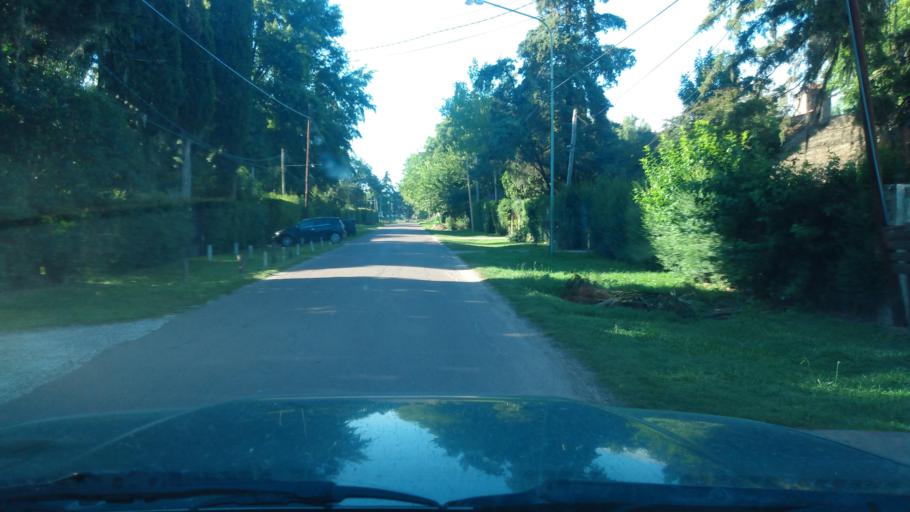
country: AR
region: Buenos Aires
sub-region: Partido de Lujan
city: Lujan
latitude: -34.5473
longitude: -59.1395
